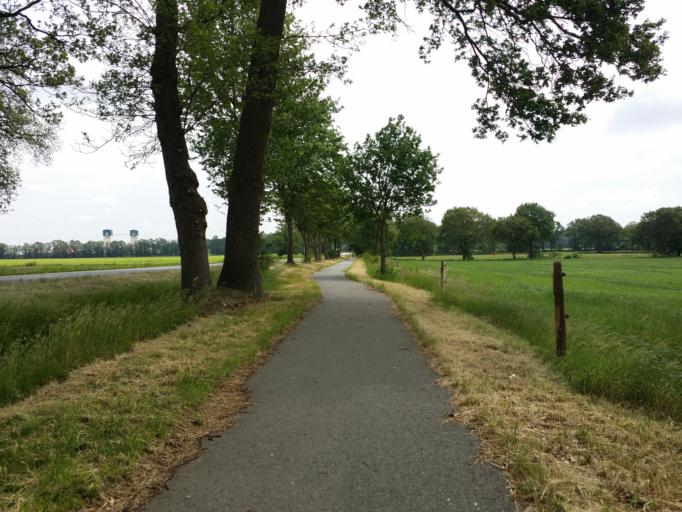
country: DE
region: Lower Saxony
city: Friedeburg
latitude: 53.4211
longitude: 7.8719
